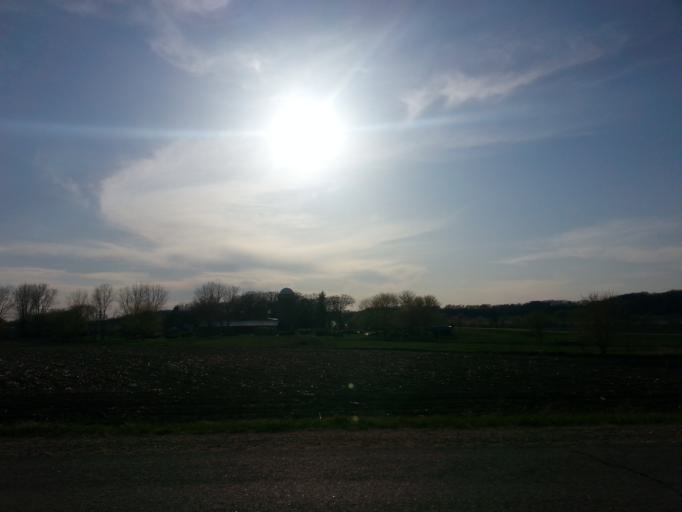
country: US
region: Wisconsin
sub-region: Pierce County
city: River Falls
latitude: 44.7646
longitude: -92.6396
